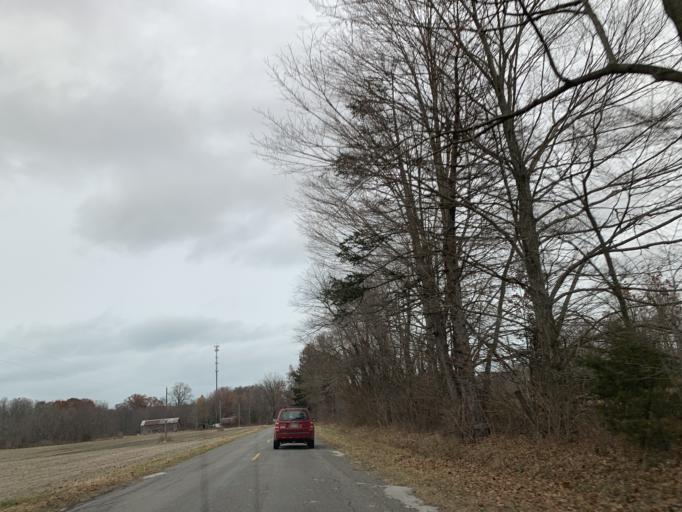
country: US
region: Michigan
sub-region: Berrien County
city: Three Oaks
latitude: 41.8199
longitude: -86.6683
